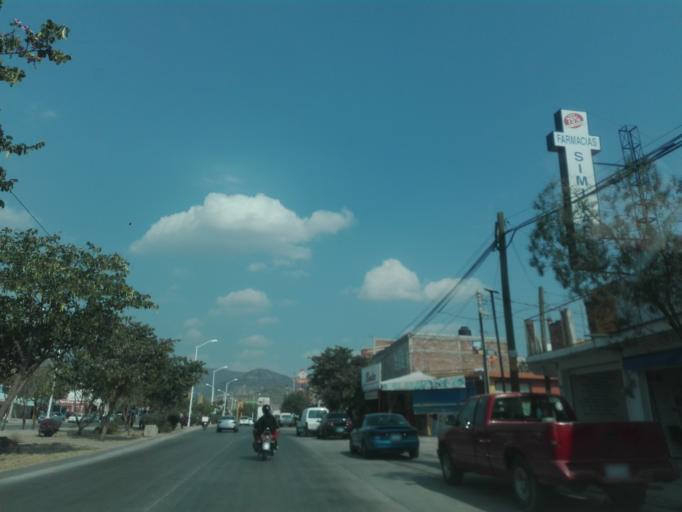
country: MX
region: Guanajuato
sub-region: Leon
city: Fraccionamiento Paraiso Real
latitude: 21.1164
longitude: -101.6025
